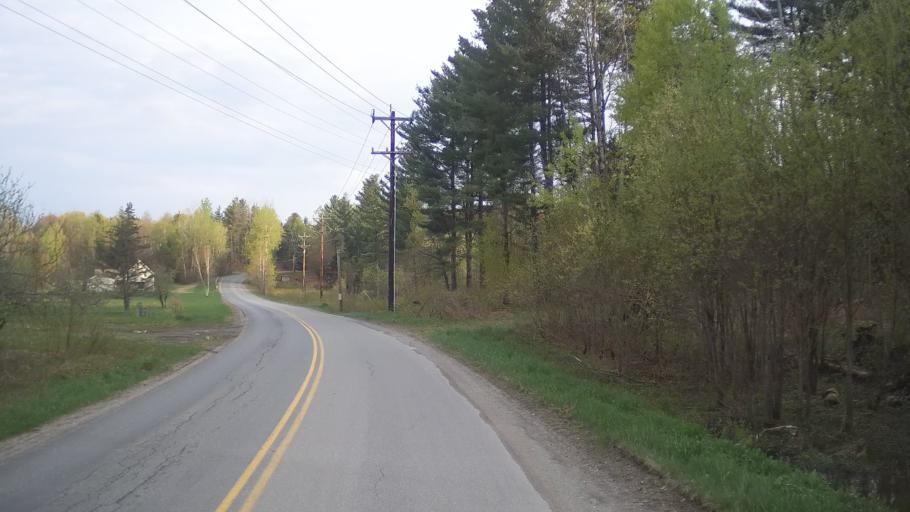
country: US
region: Vermont
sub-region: Orleans County
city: Newport
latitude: 44.9459
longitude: -72.4382
